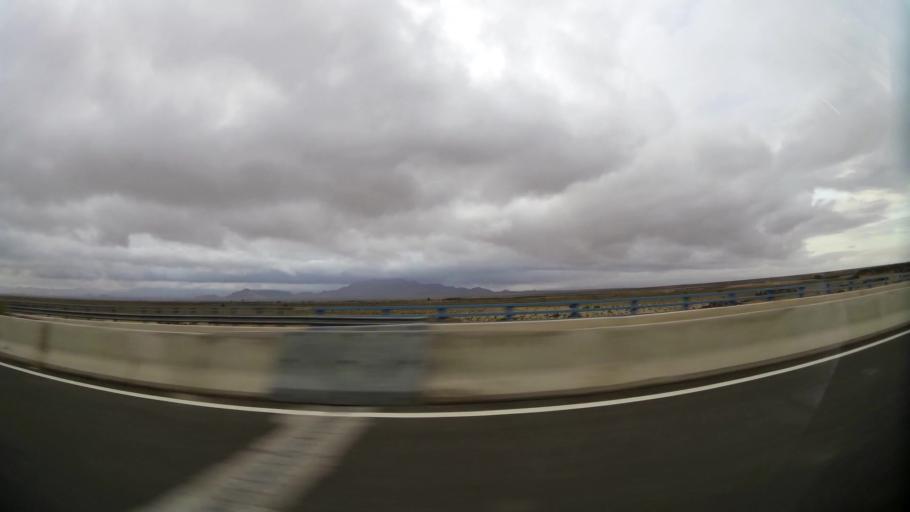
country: MA
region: Taza-Al Hoceima-Taounate
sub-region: Taza
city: Guercif
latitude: 34.3834
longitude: -3.2339
